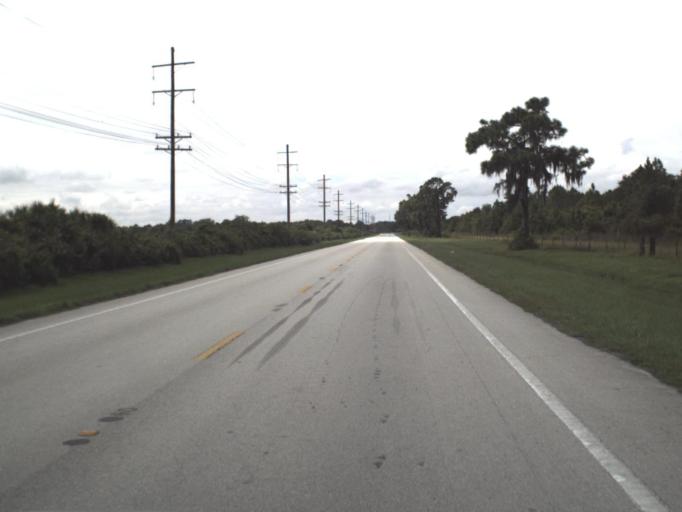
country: US
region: Florida
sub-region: Hillsborough County
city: Wimauma
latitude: 27.5893
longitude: -82.1105
